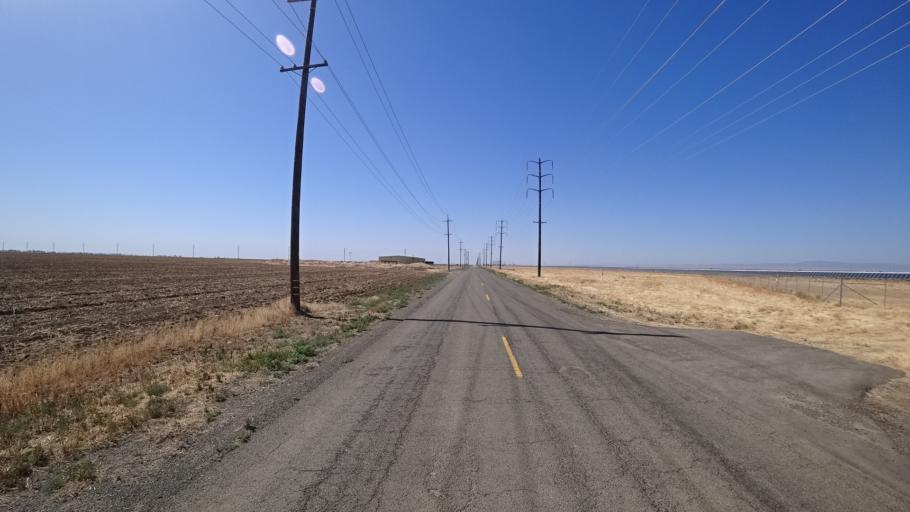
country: US
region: California
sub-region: Kings County
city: Lemoore Station
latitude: 36.2311
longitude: -119.9053
